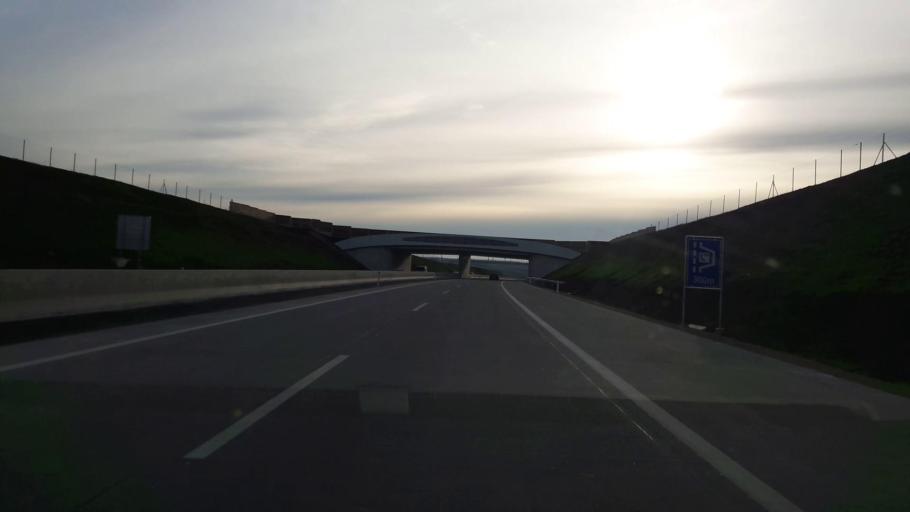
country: AT
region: Lower Austria
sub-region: Politischer Bezirk Mistelbach
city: Wilfersdorf
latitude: 48.5880
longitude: 16.6280
